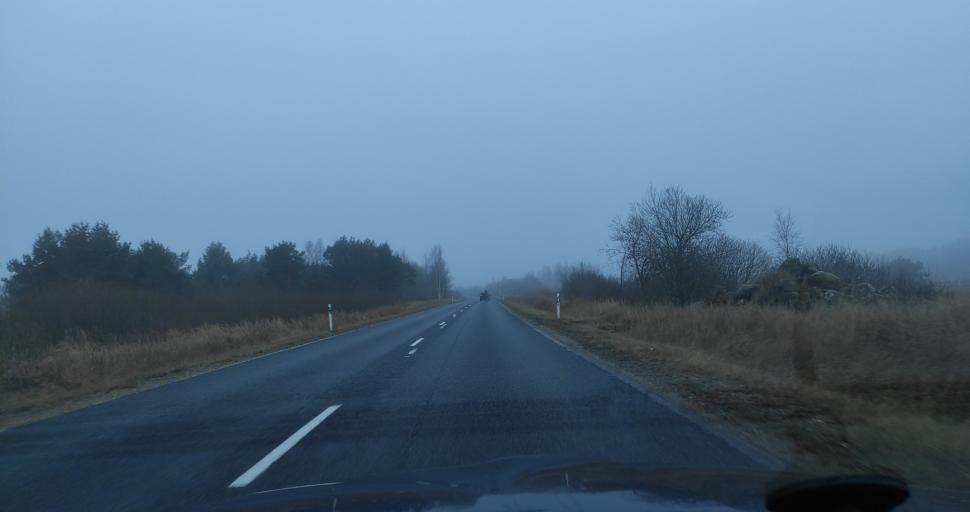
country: LV
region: Alsunga
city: Alsunga
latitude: 57.1172
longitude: 21.4241
